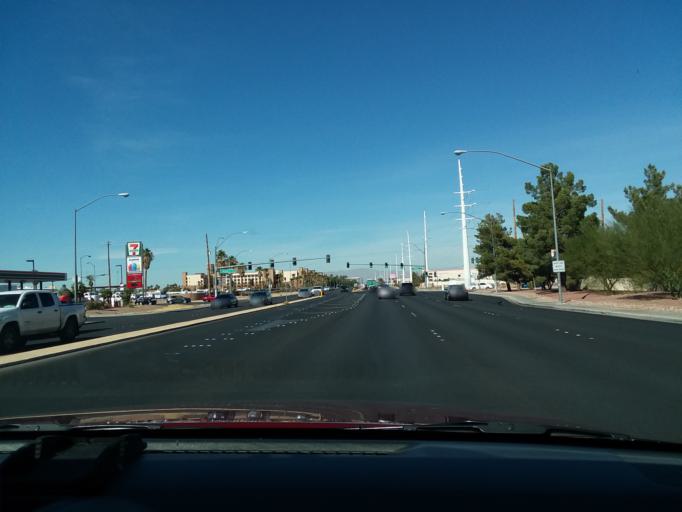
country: US
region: Nevada
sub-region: Clark County
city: Enterprise
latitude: 36.0270
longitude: -115.1719
